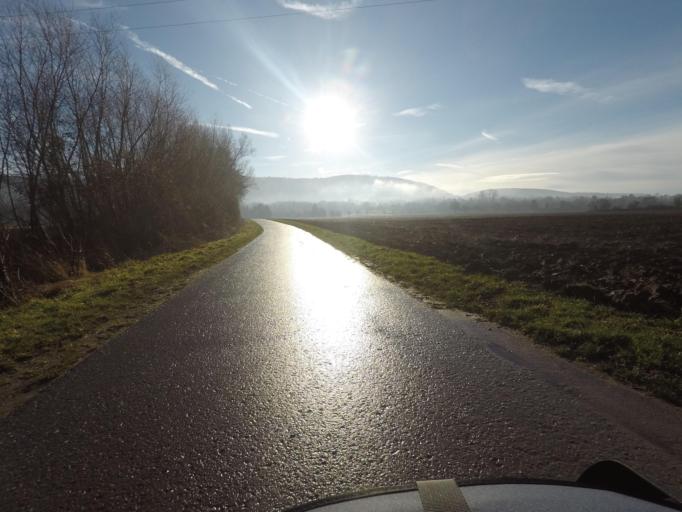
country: DE
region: Baden-Wuerttemberg
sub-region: Karlsruhe Region
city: Ettlingen
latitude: 48.9605
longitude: 8.4190
